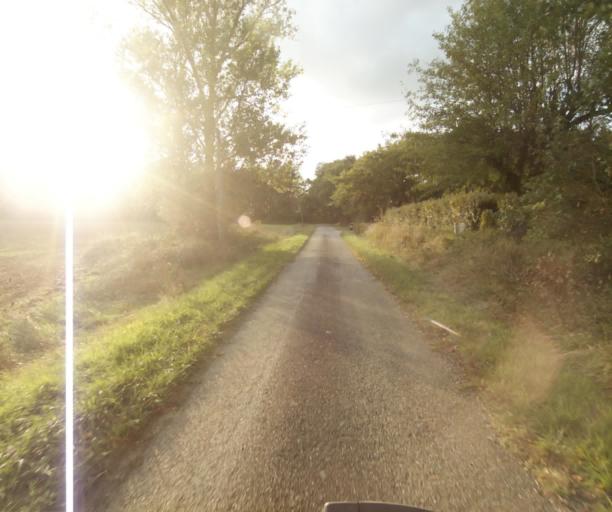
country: FR
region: Midi-Pyrenees
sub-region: Departement de la Haute-Garonne
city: Launac
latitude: 43.8305
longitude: 1.1224
